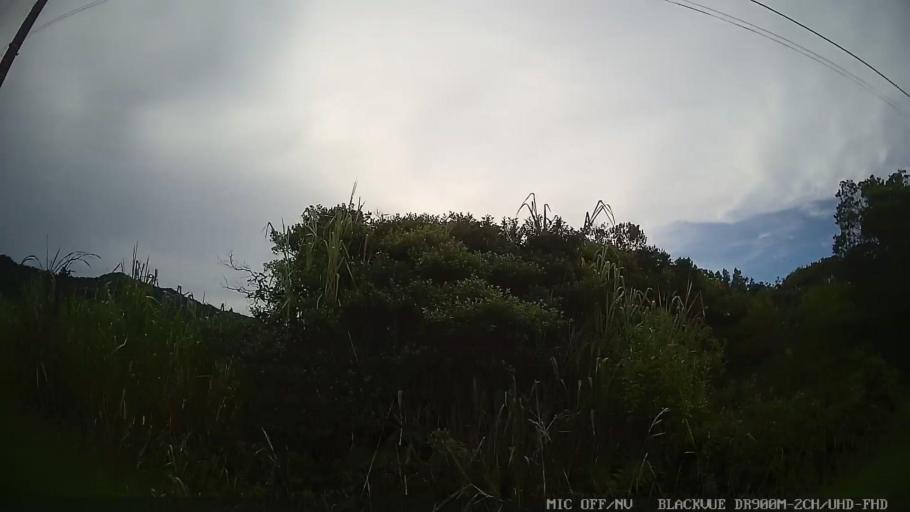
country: BR
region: Sao Paulo
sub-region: Iguape
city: Iguape
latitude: -24.6837
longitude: -47.4681
